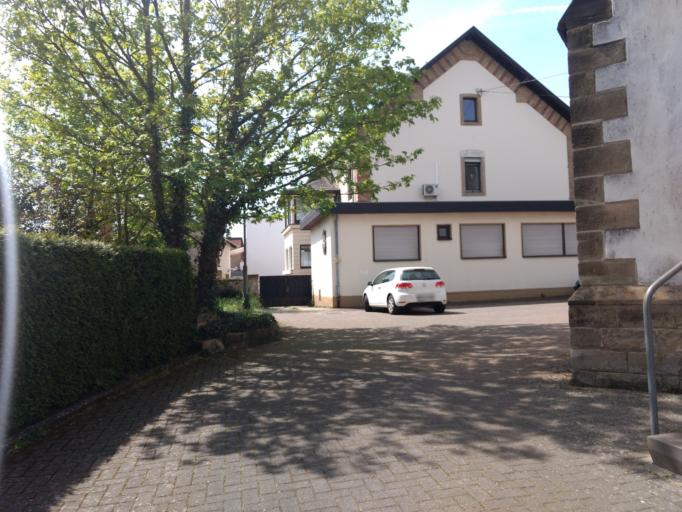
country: DE
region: Saarland
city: Schwalbach
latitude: 49.3037
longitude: 6.8162
